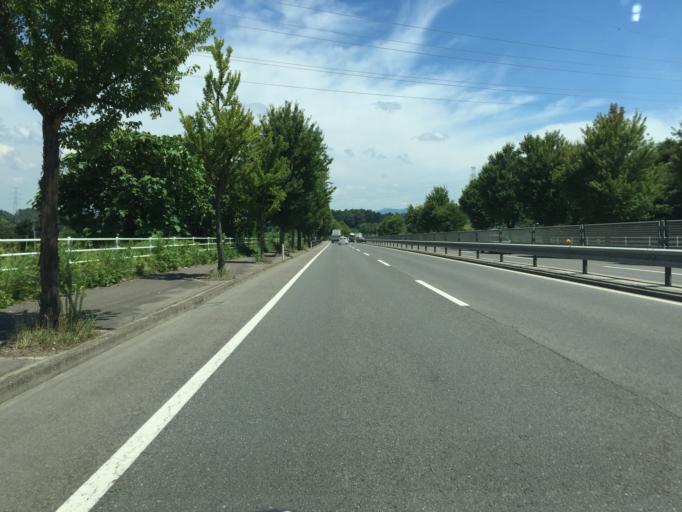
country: JP
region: Fukushima
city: Fukushima-shi
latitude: 37.6850
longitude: 140.4702
